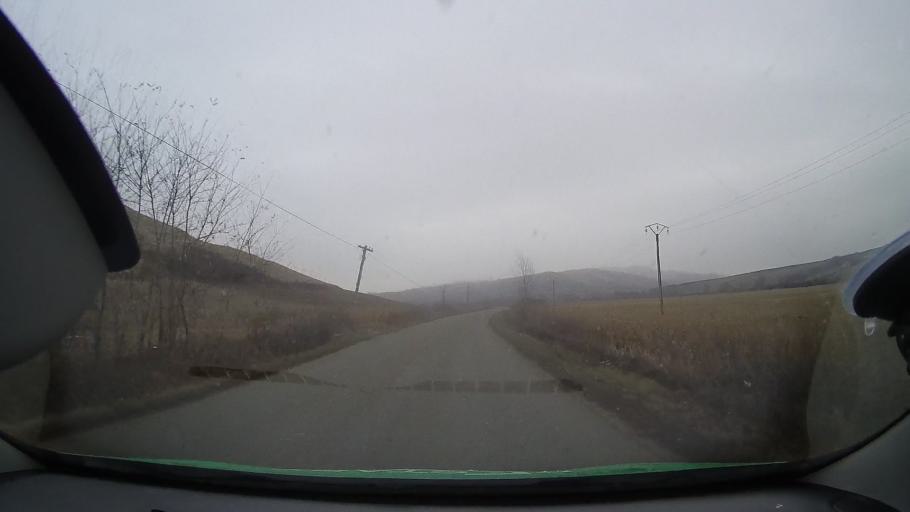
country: RO
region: Alba
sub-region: Comuna Farau
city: Farau
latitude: 46.3347
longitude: 23.9677
